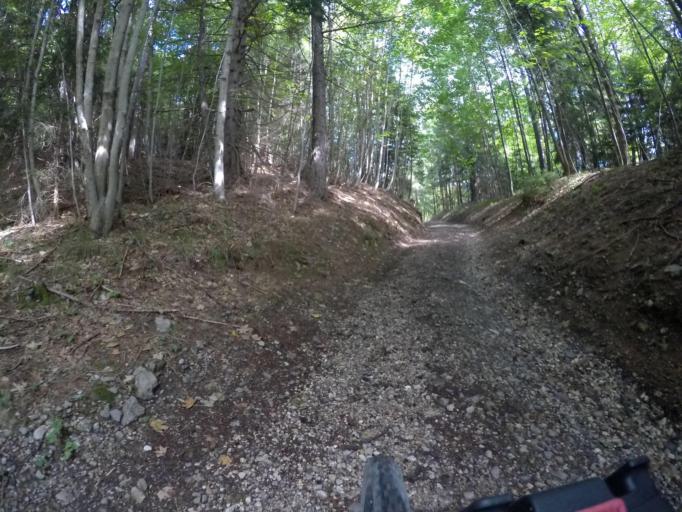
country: IT
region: Friuli Venezia Giulia
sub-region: Provincia di Udine
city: Paularo
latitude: 46.4941
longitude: 13.1860
